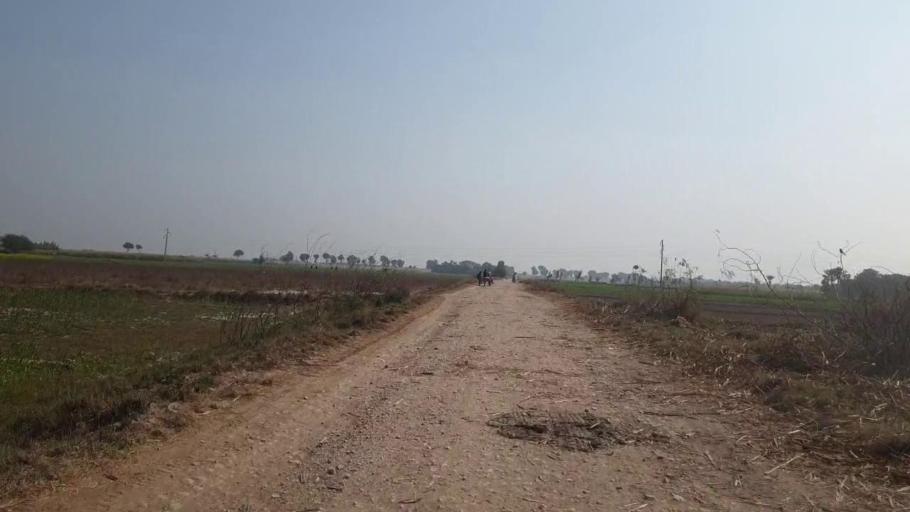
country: PK
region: Sindh
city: Bhit Shah
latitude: 25.7183
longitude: 68.5438
